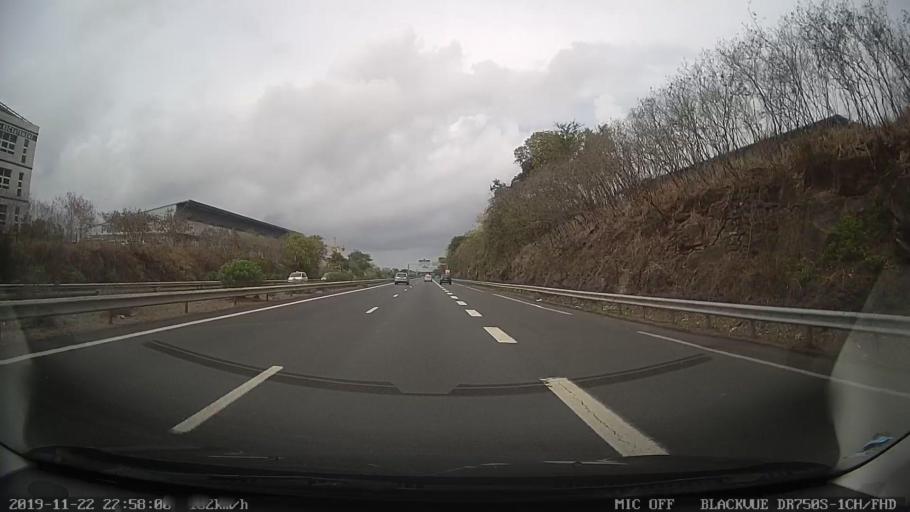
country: RE
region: Reunion
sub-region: Reunion
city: La Possession
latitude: -20.9358
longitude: 55.3307
